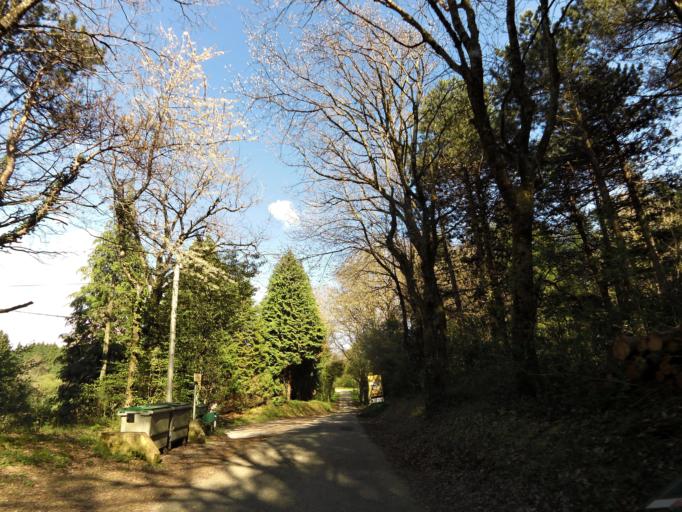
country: FR
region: Midi-Pyrenees
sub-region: Departement du Tarn
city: Soreze
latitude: 43.3941
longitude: 2.0900
